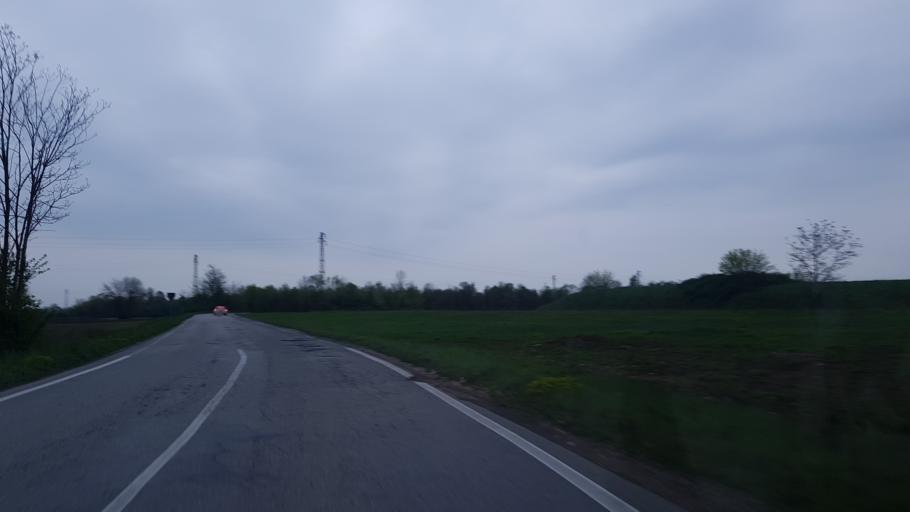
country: IT
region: Friuli Venezia Giulia
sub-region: Provincia di Udine
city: Palmanova
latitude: 45.9027
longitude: 13.3193
